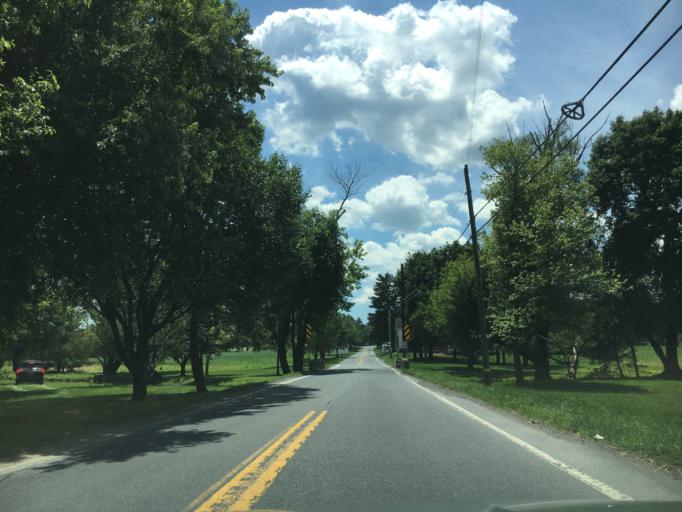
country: US
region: Pennsylvania
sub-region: Lehigh County
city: Schnecksville
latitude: 40.6560
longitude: -75.5761
